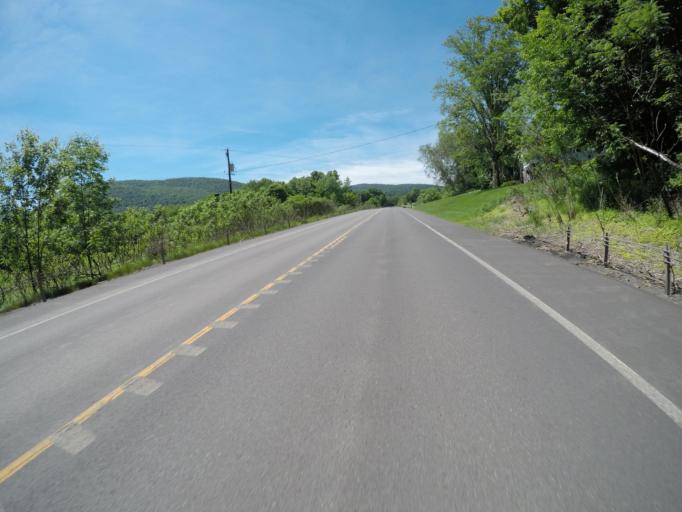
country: US
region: New York
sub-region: Delaware County
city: Walton
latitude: 42.1758
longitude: -75.0233
